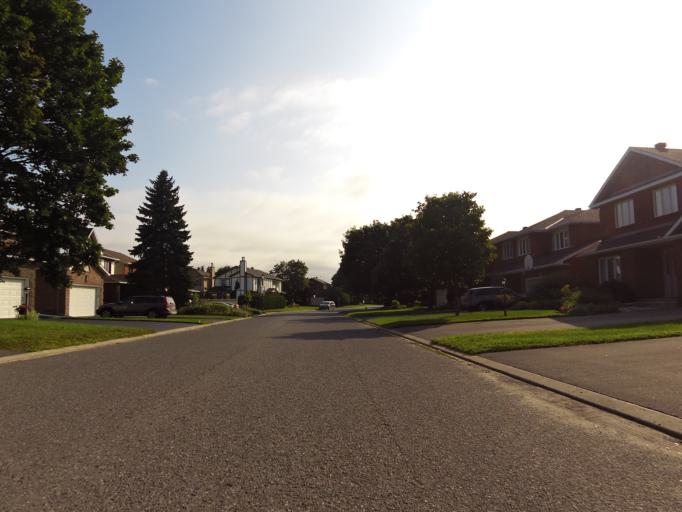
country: CA
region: Ontario
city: Bells Corners
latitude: 45.3433
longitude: -75.7756
